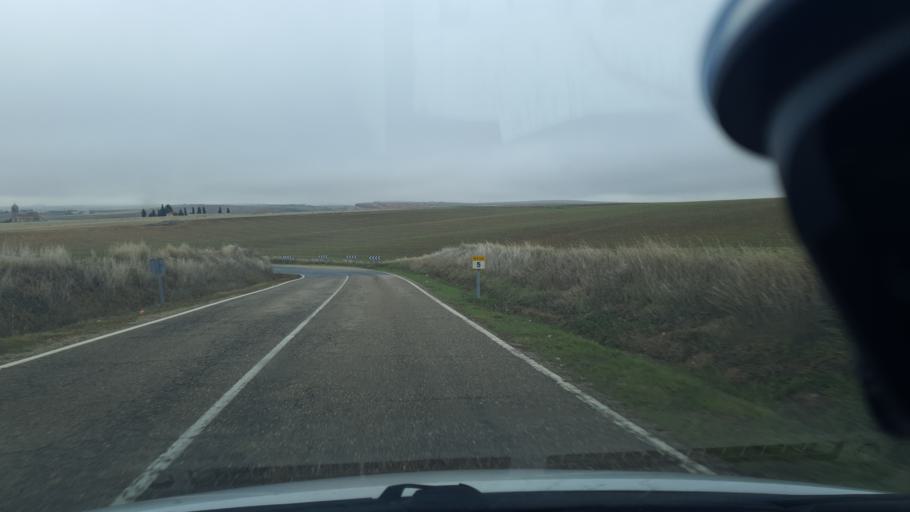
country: ES
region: Castille and Leon
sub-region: Provincia de Segovia
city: Valseca
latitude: 40.9943
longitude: -4.1863
